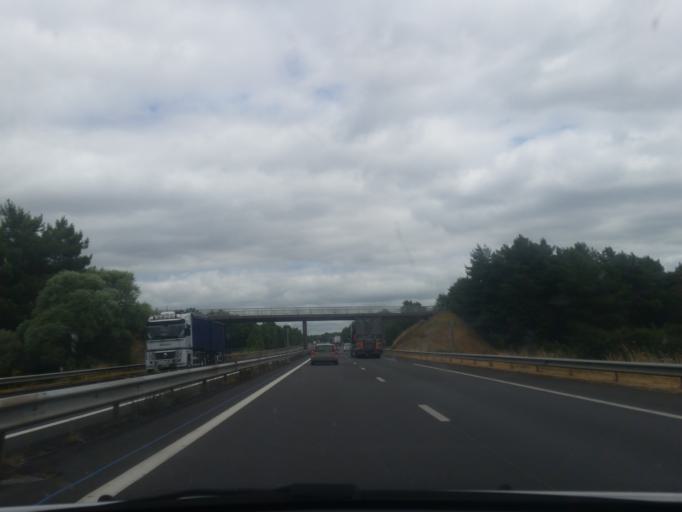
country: FR
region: Pays de la Loire
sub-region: Departement de Maine-et-Loire
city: Seiches-sur-le-Loir
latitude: 47.6154
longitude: -0.2914
